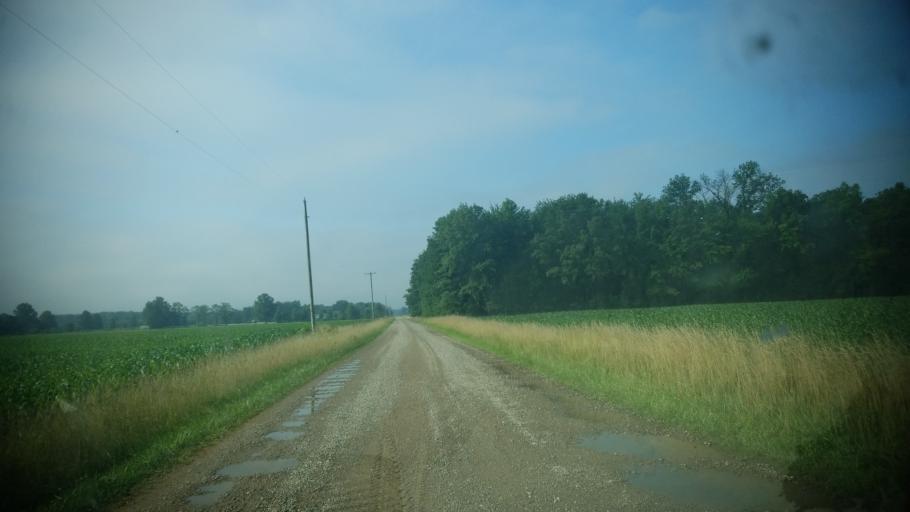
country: US
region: Illinois
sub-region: Clay County
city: Flora
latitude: 38.6013
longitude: -88.3642
